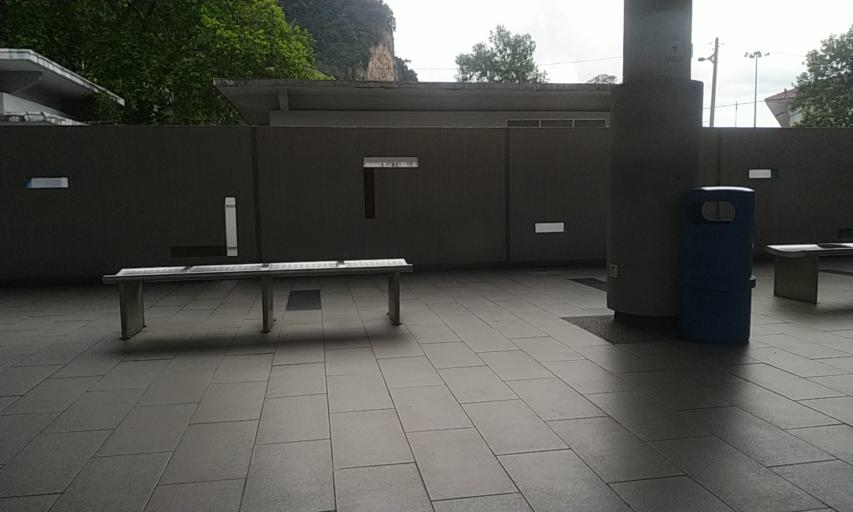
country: MY
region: Kuala Lumpur
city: Kuala Lumpur
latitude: 3.2373
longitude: 101.6813
